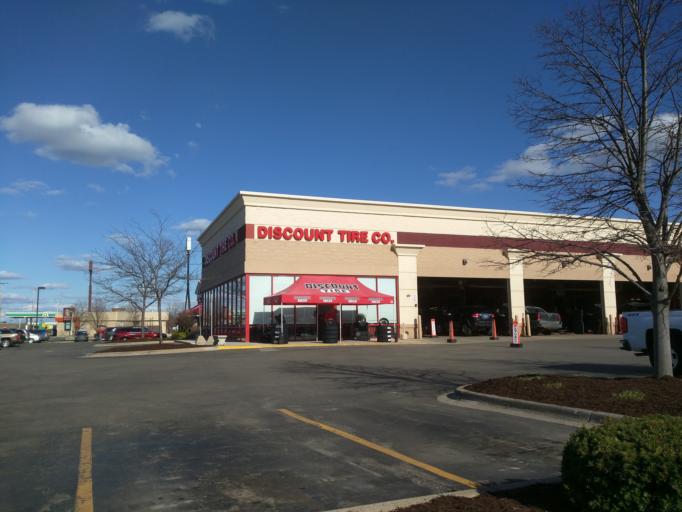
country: US
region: Michigan
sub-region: Eaton County
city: Waverly
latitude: 42.7407
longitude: -84.6747
